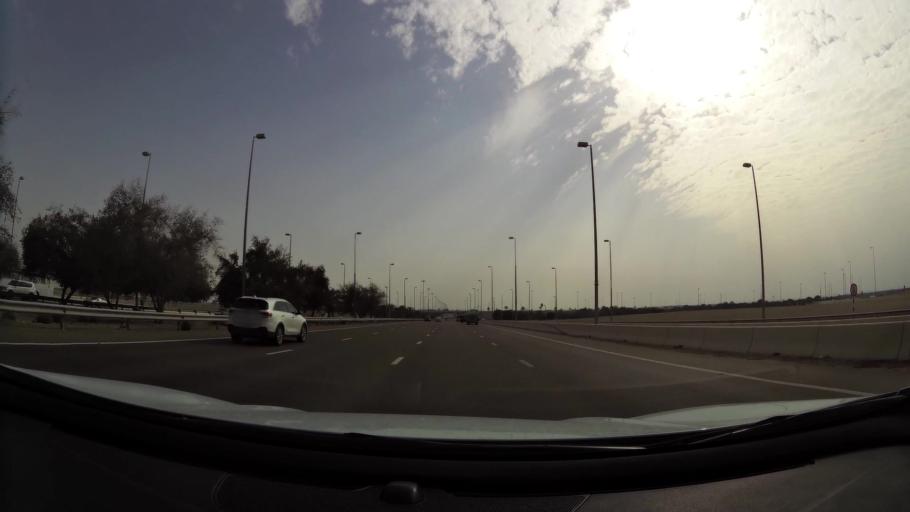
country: AE
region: Abu Dhabi
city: Abu Dhabi
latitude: 24.4145
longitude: 54.6749
